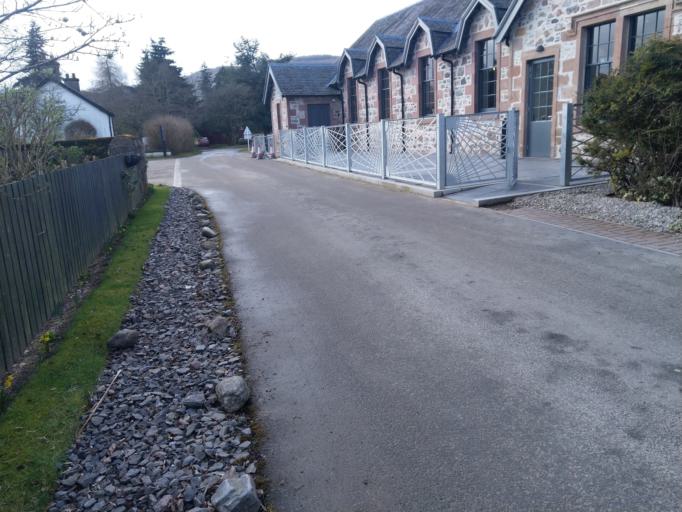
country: GB
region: Scotland
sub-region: Highland
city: Inverness
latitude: 57.4329
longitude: -4.3037
